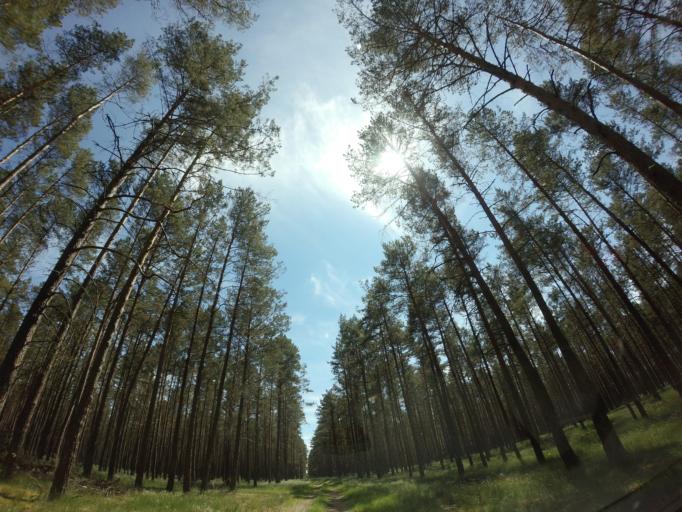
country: PL
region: West Pomeranian Voivodeship
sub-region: Powiat drawski
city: Kalisz Pomorski
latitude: 53.1826
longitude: 15.8998
